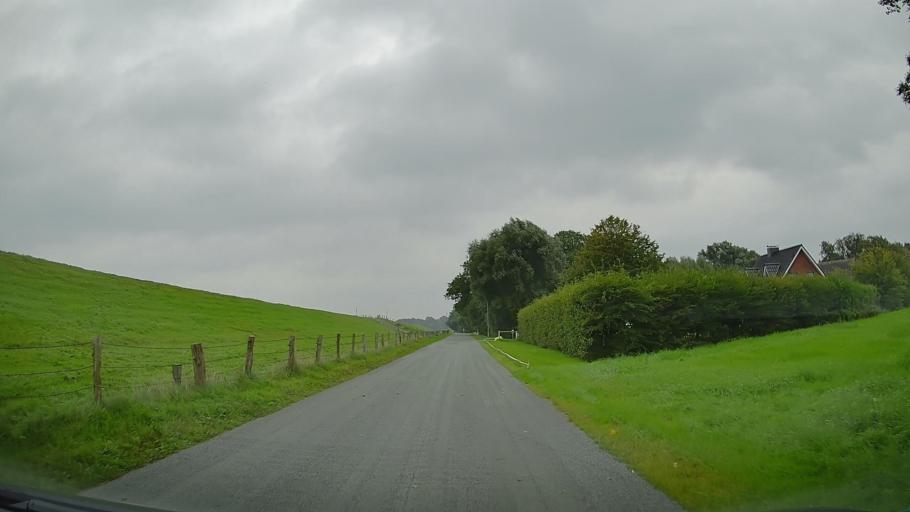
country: DE
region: Lower Saxony
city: Belum
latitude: 53.8227
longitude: 9.0152
